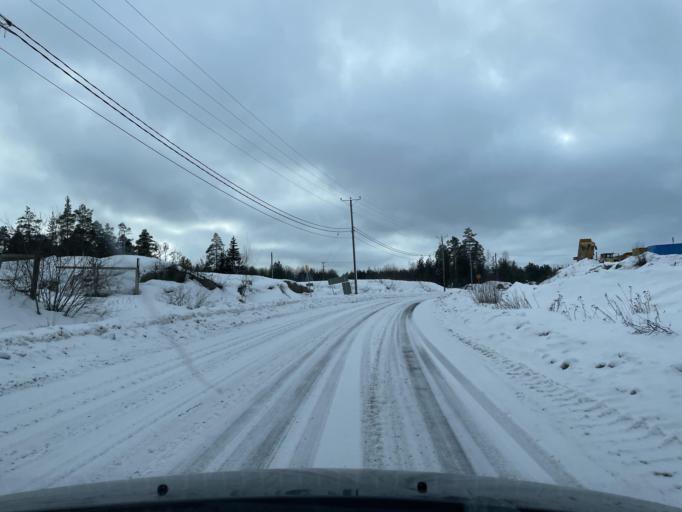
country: FI
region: Uusimaa
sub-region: Helsinki
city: Espoo
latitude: 60.2417
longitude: 24.5599
